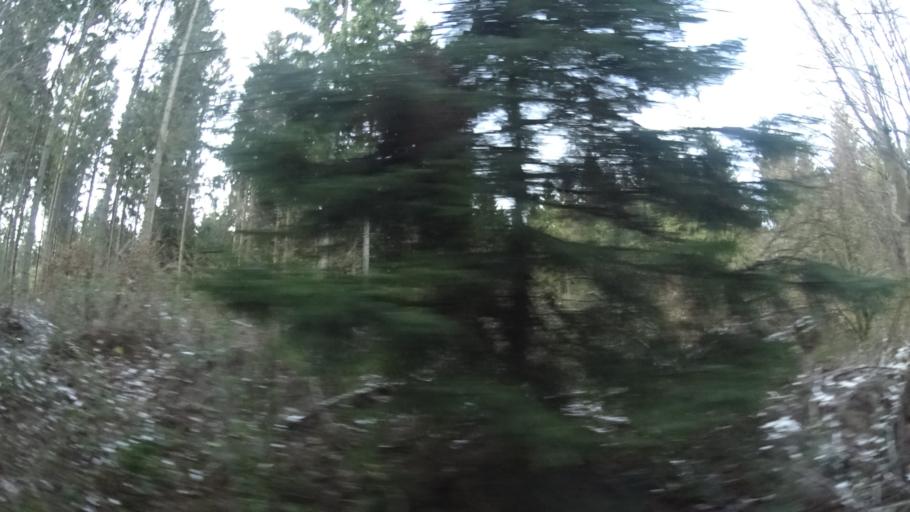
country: DE
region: Thuringia
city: Friedrichroda
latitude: 50.8306
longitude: 10.5539
